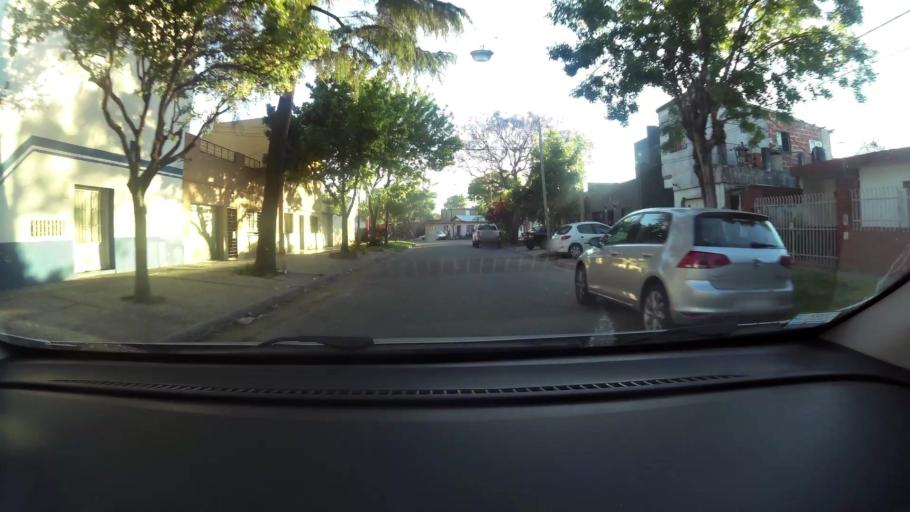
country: AR
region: Santa Fe
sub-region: Departamento de Rosario
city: Rosario
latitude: -32.9694
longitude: -60.6716
